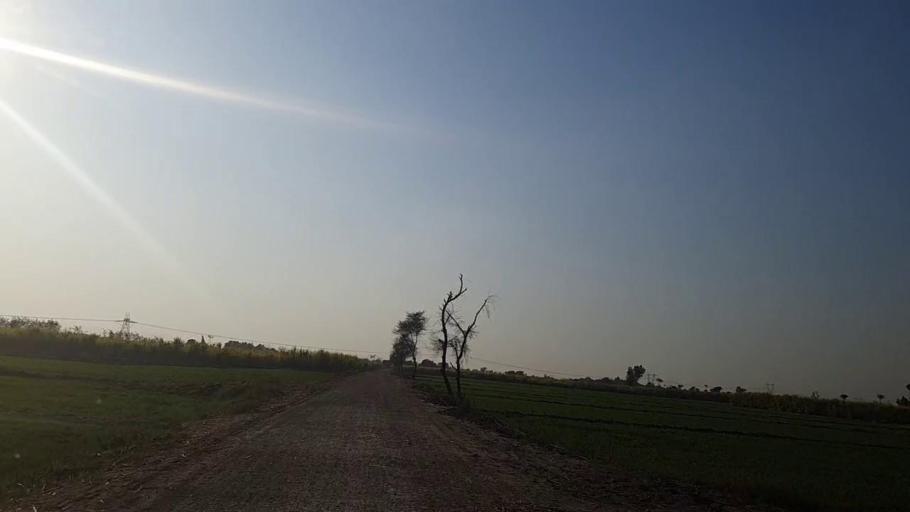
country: PK
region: Sindh
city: Sakrand
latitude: 26.3111
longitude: 68.1561
